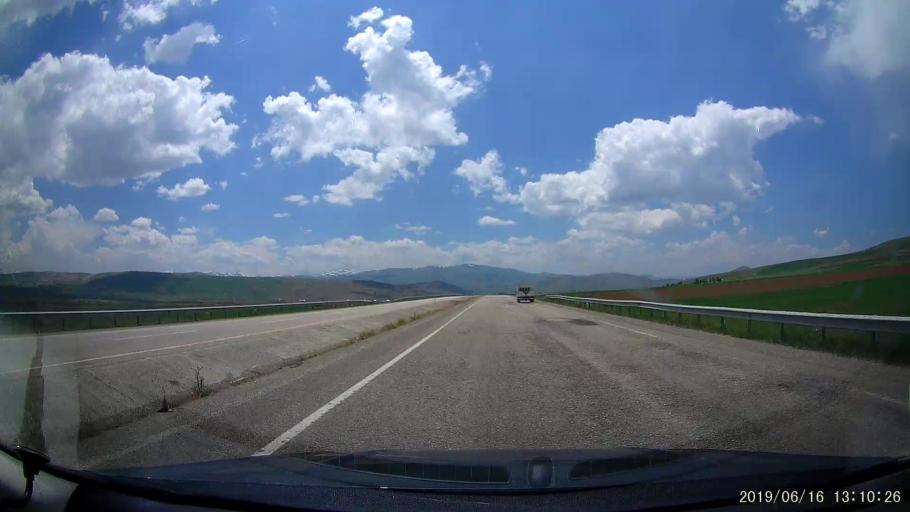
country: TR
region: Agri
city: Diyadin
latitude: 39.5952
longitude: 43.6329
